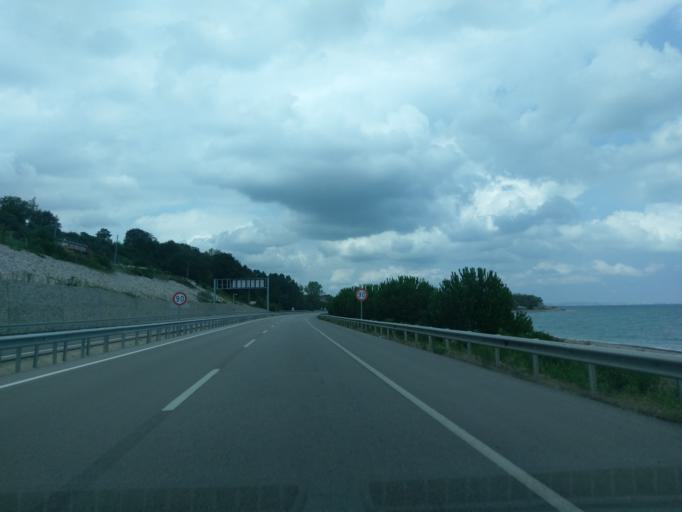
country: TR
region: Sinop
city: Gerze
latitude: 41.8288
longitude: 35.1619
